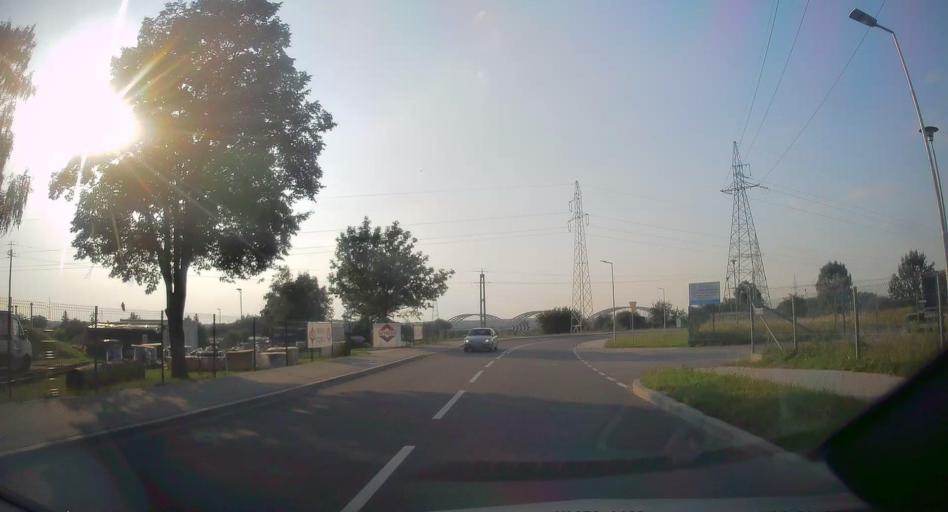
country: PL
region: Subcarpathian Voivodeship
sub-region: Powiat debicki
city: Debica
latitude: 50.0431
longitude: 21.3814
